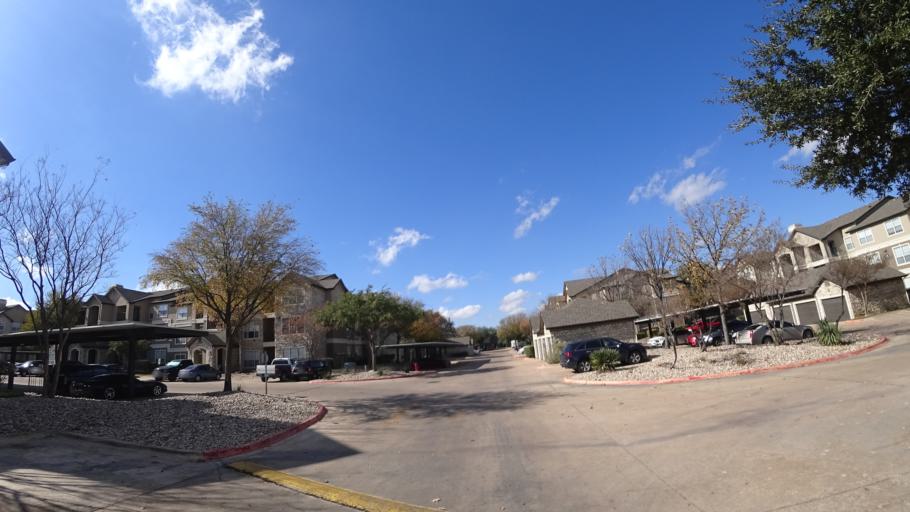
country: US
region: Texas
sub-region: Travis County
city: Wells Branch
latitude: 30.4395
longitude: -97.6900
